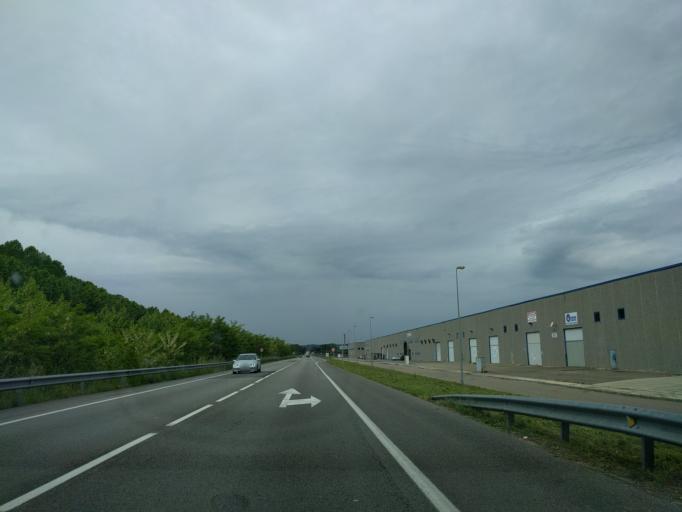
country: ES
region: Catalonia
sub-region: Provincia de Girona
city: Breda
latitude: 41.7289
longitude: 2.5857
